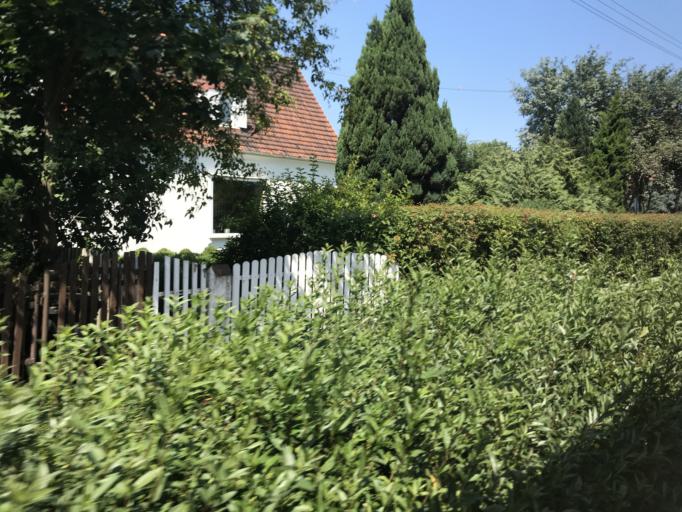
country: PL
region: Pomeranian Voivodeship
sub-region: Gdansk
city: Gdansk
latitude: 54.4036
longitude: 18.6328
